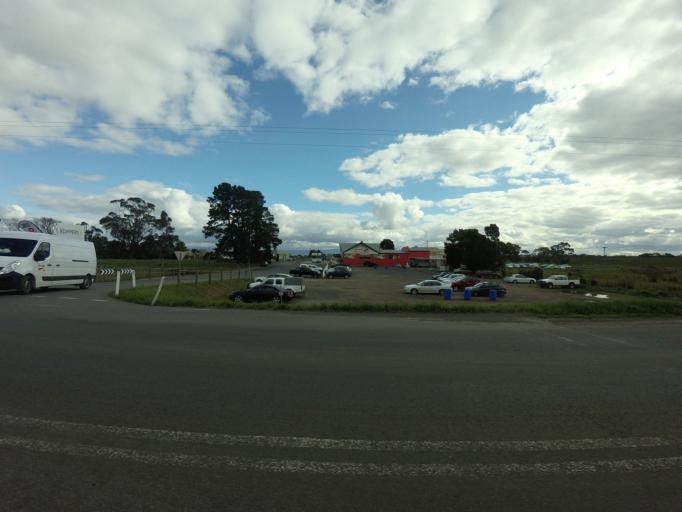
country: AU
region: Tasmania
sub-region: Northern Midlands
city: Longford
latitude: -41.5861
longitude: 147.1176
